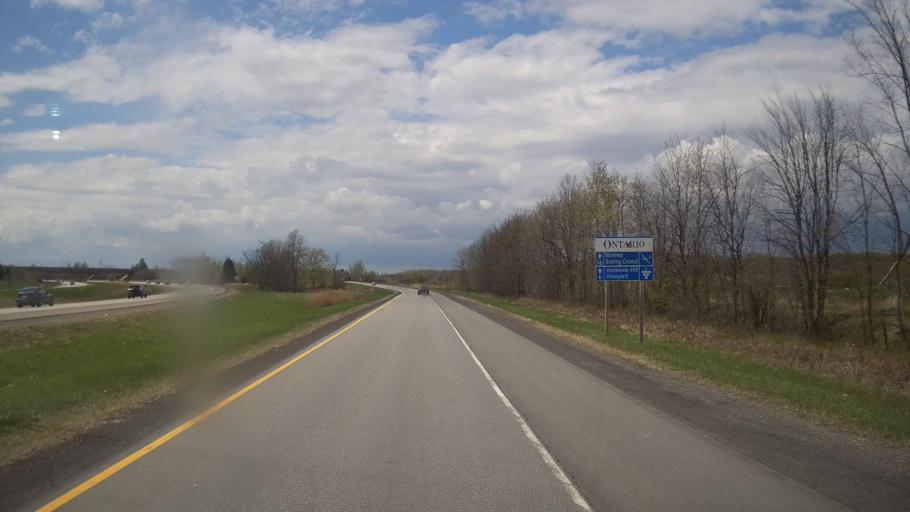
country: CA
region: Ontario
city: Hawkesbury
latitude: 45.5655
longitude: -74.4981
